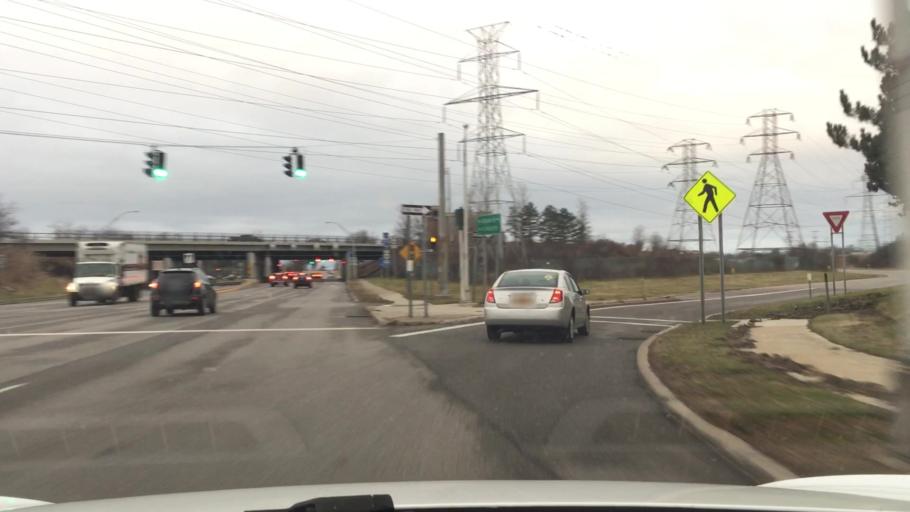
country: US
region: New York
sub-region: Erie County
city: Amherst
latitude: 42.9786
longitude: -78.7813
